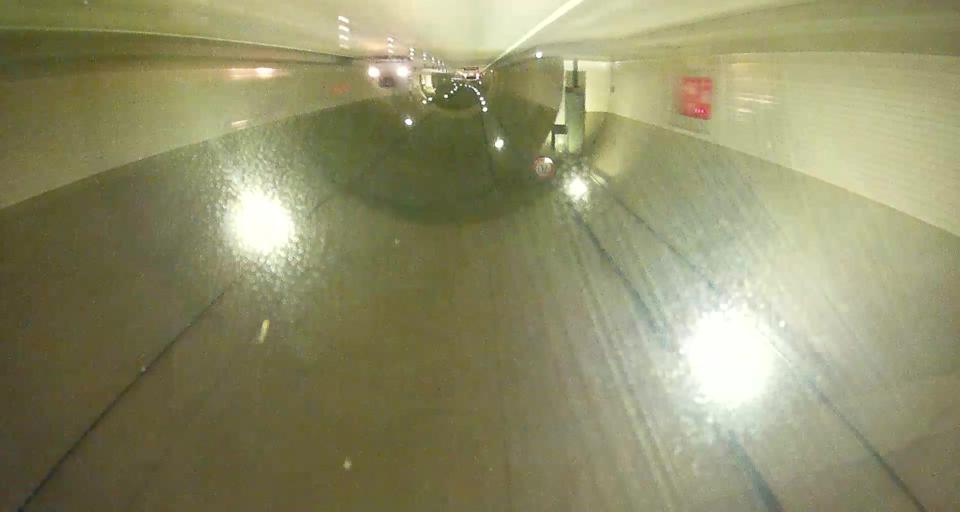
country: JP
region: Iwate
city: Miyako
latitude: 39.9315
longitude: 141.8558
